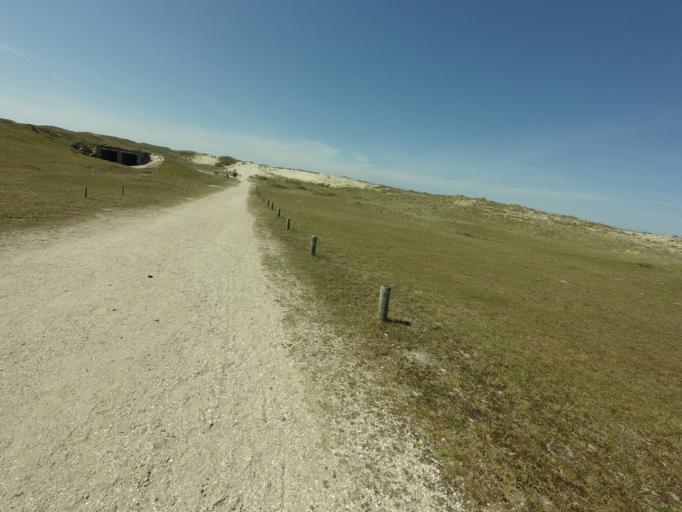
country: NL
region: Zeeland
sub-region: Gemeente Middelburg
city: Middelburg
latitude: 51.5766
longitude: 3.5279
